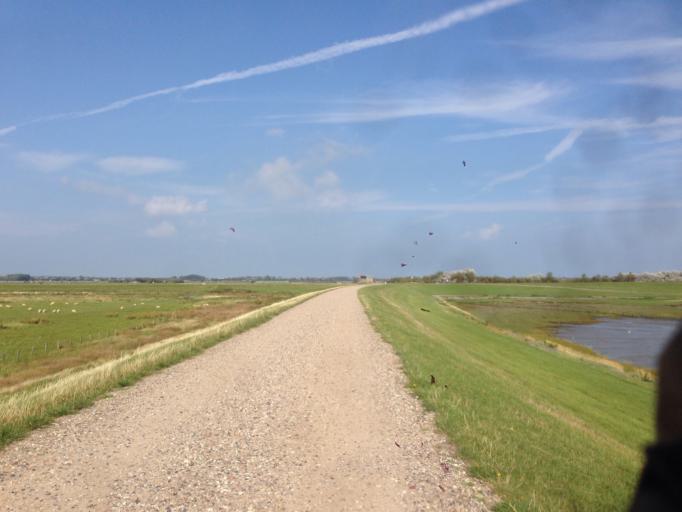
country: DE
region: Schleswig-Holstein
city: Tinnum
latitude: 54.8801
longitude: 8.3386
